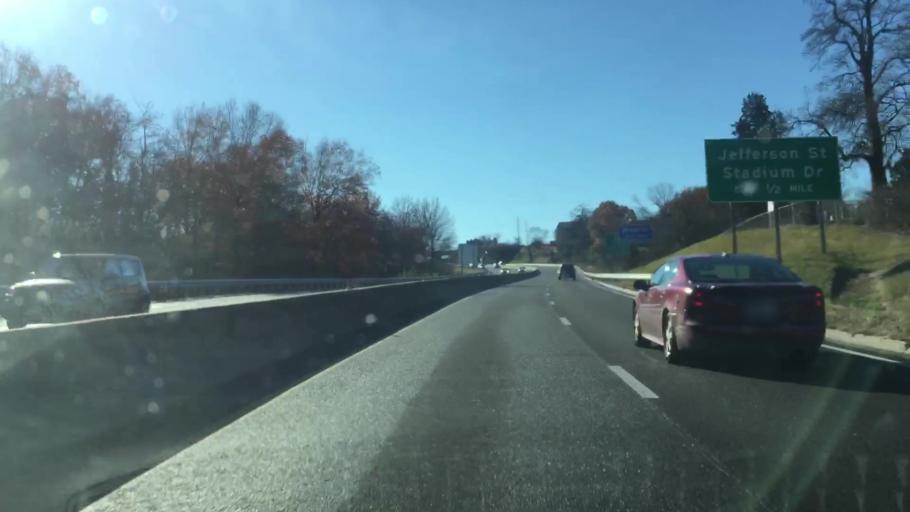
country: US
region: Missouri
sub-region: Cole County
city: Jefferson City
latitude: 38.5706
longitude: -92.1839
